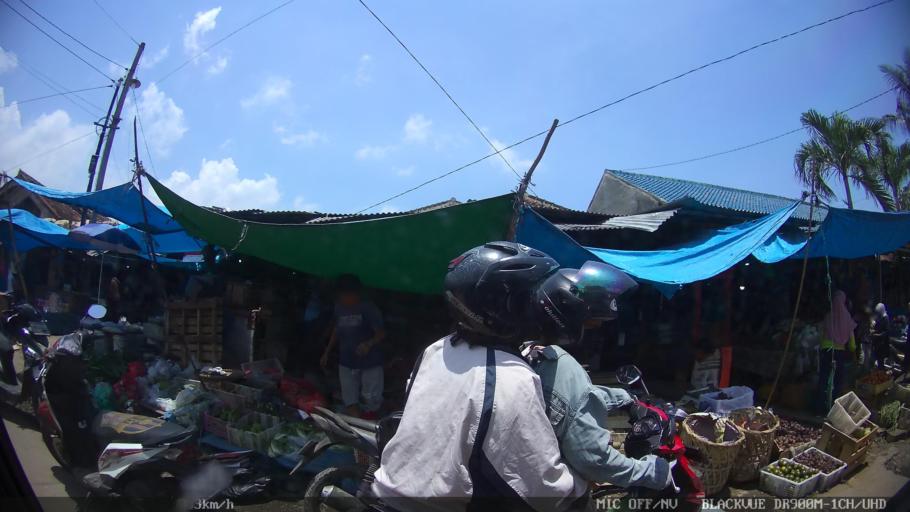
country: ID
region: Lampung
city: Kedaton
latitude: -5.3831
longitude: 105.2939
